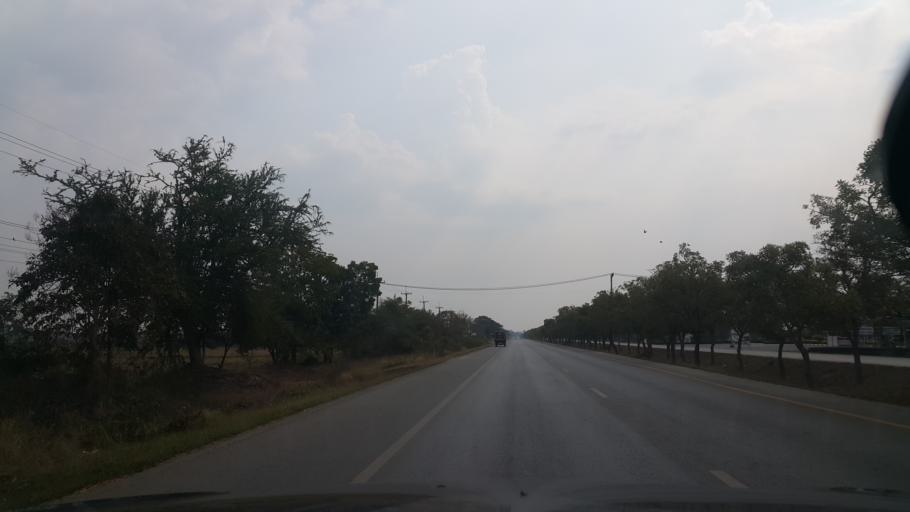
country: TH
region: Sukhothai
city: Sukhothai
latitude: 17.0631
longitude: 99.8810
